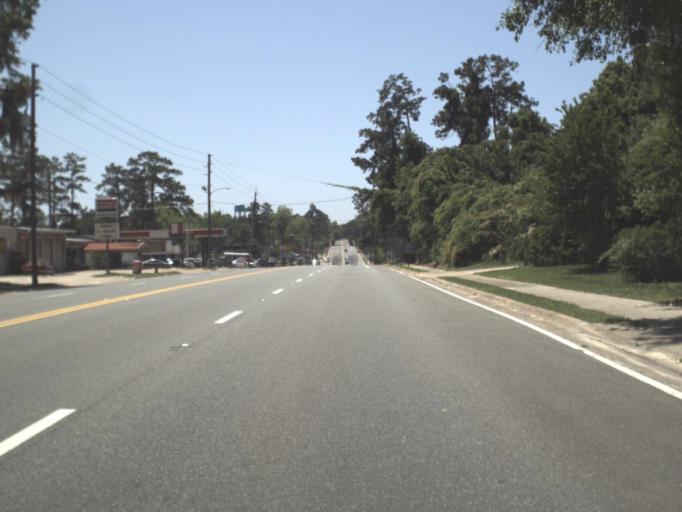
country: US
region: Florida
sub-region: Jefferson County
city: Monticello
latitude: 30.5574
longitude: -83.8702
